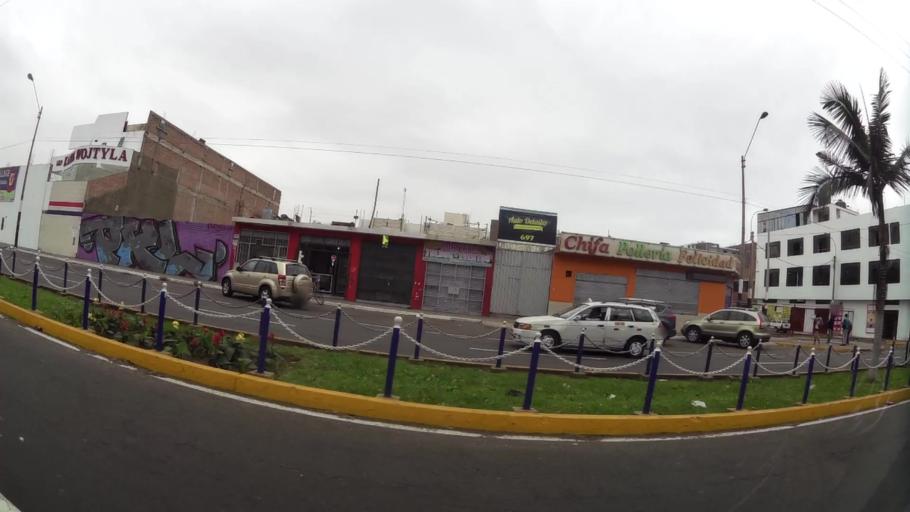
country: PE
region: Lima
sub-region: Lima
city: Surco
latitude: -12.1977
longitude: -77.0117
